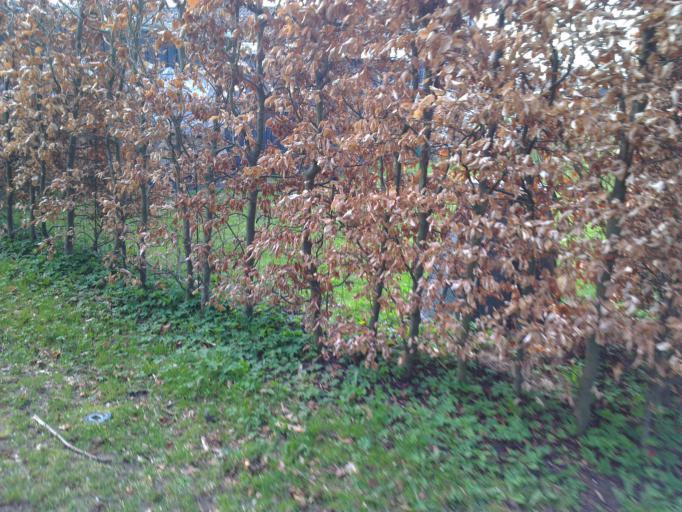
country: DK
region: Capital Region
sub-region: Frederikssund Kommune
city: Jaegerspris
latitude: 55.8342
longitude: 11.9660
